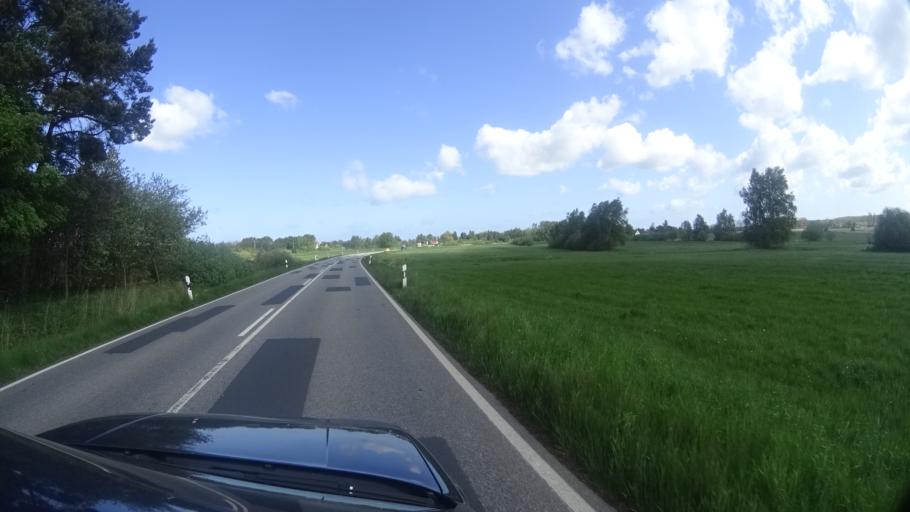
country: DE
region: Mecklenburg-Vorpommern
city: Barth
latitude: 54.3713
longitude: 12.6726
